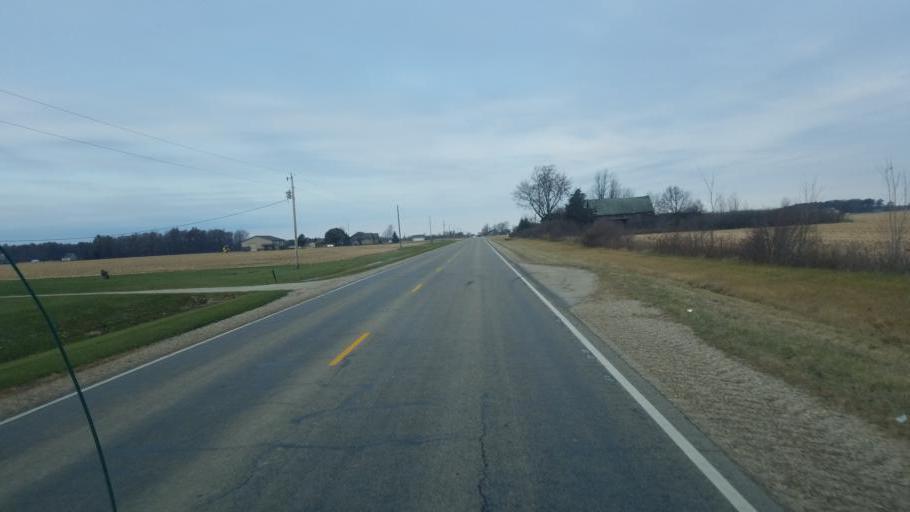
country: US
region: Indiana
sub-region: Adams County
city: Geneva
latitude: 40.5425
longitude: -84.8683
